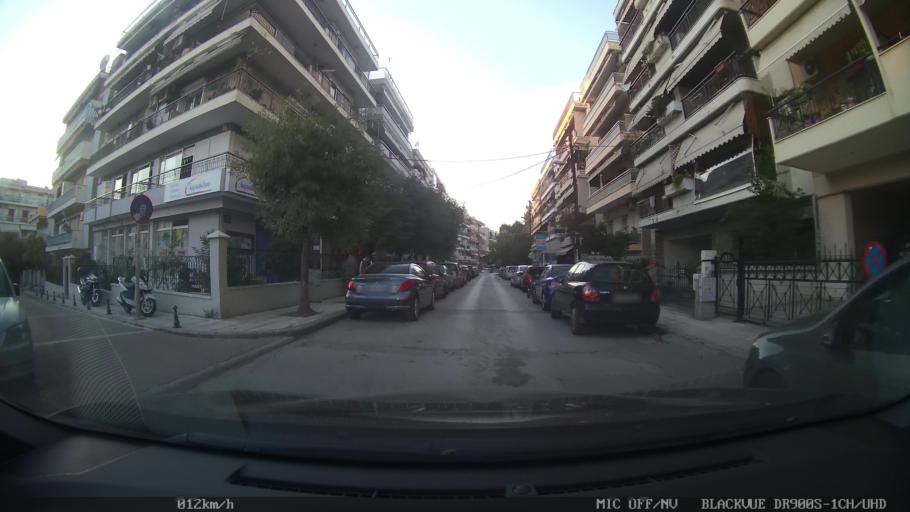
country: GR
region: Central Macedonia
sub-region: Nomos Thessalonikis
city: Triandria
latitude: 40.6102
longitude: 22.9860
